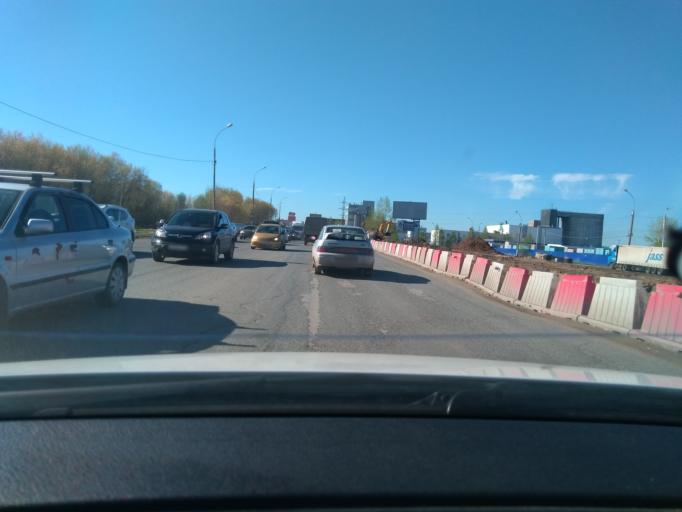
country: RU
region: Perm
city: Froly
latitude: 57.9510
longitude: 56.2651
